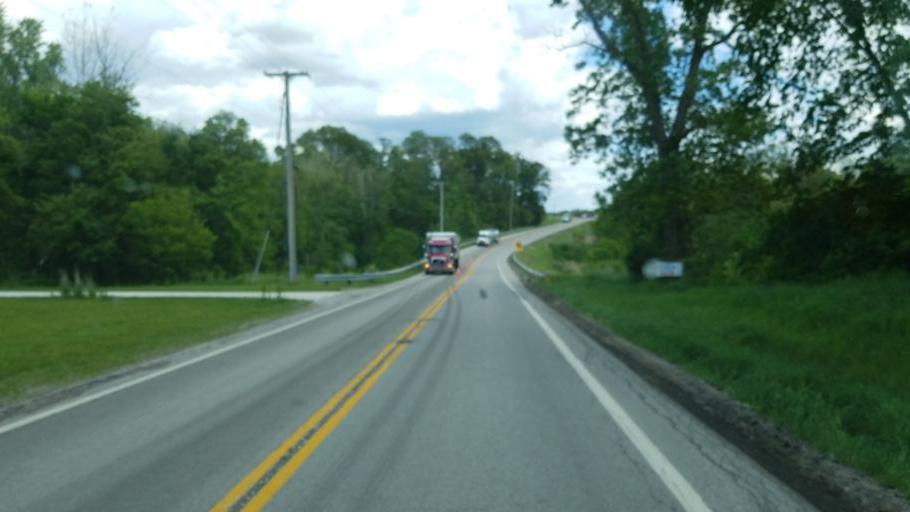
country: US
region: Ohio
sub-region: Erie County
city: Milan
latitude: 41.2954
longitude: -82.6534
